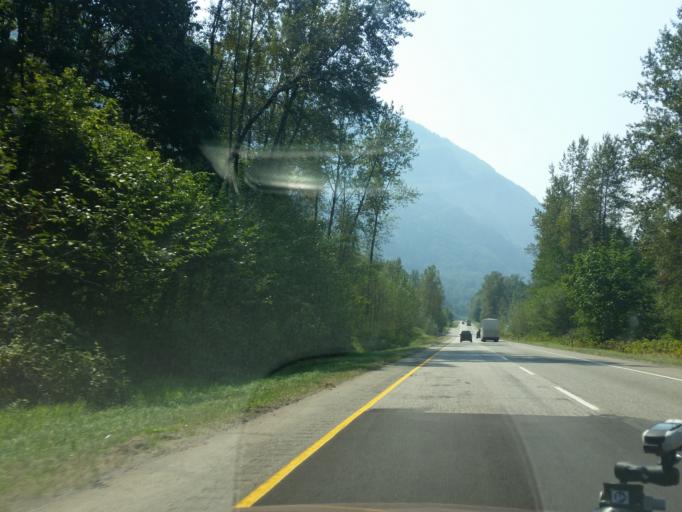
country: CA
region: British Columbia
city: Agassiz
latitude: 49.2308
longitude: -121.6838
